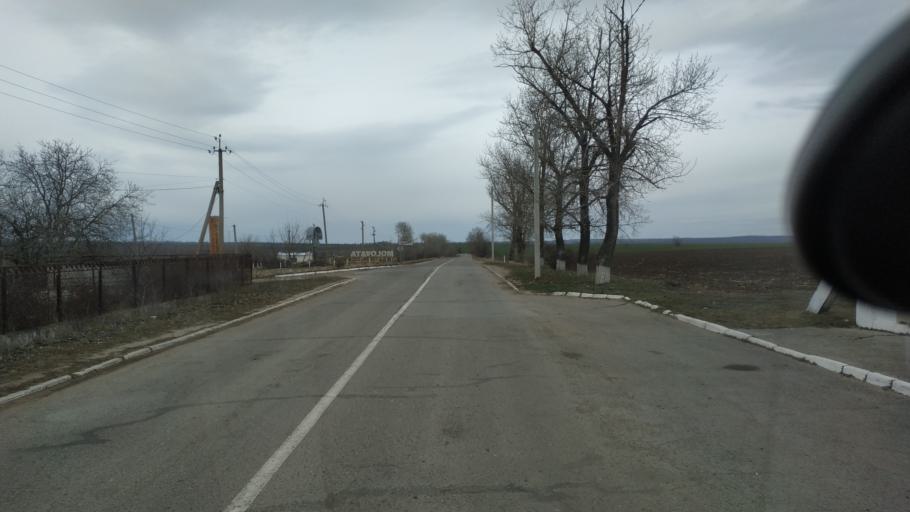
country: MD
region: Telenesti
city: Cocieri
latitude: 47.3566
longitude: 29.1163
